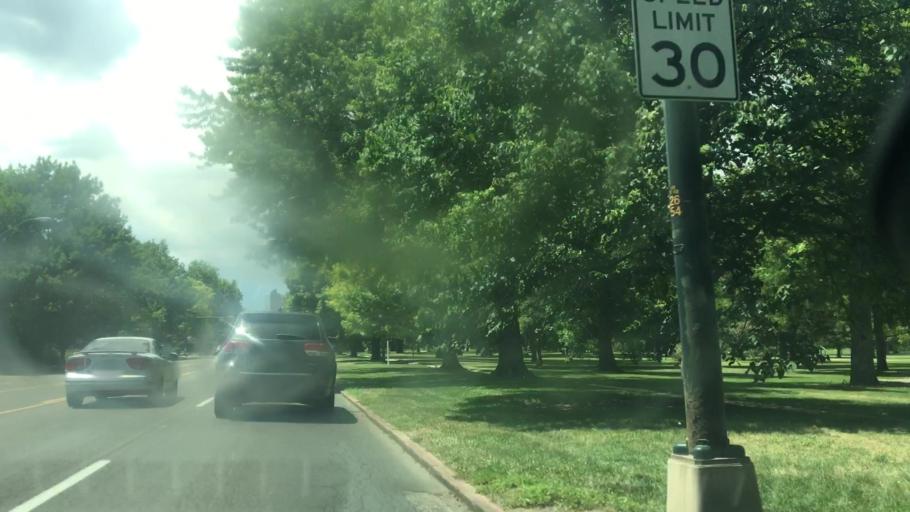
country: US
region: Colorado
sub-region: Denver County
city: Denver
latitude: 39.7439
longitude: -104.9518
